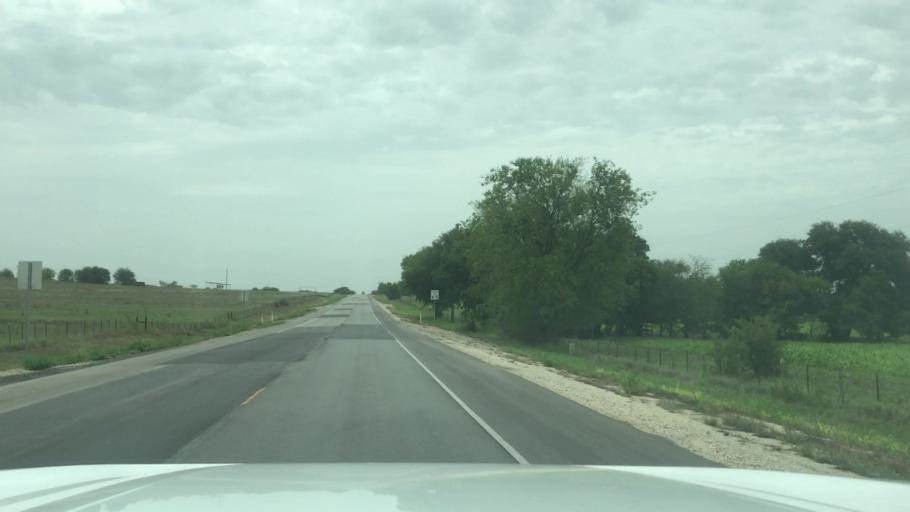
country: US
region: Texas
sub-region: Erath County
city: Dublin
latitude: 32.0685
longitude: -98.2189
